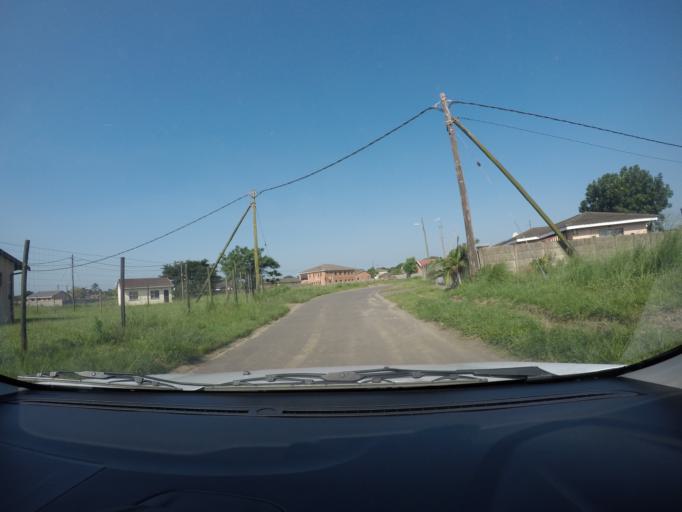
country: ZA
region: KwaZulu-Natal
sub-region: uThungulu District Municipality
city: Richards Bay
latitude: -28.7221
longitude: 32.0353
